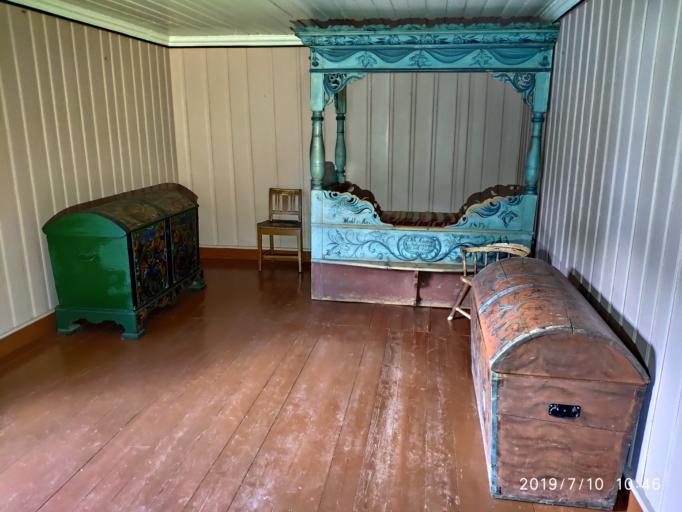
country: NO
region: Telemark
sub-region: Tokke
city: Dalen
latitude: 59.4653
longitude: 8.0212
